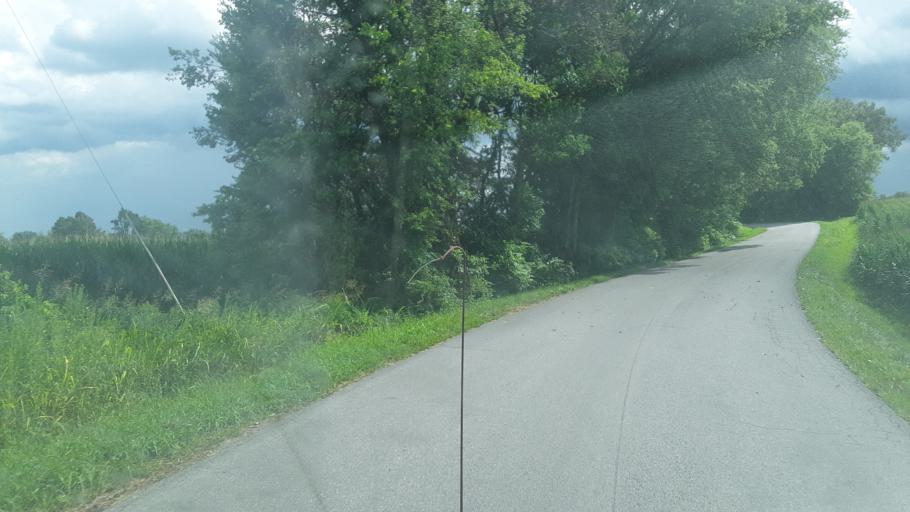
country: US
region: Kentucky
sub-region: Todd County
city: Elkton
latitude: 36.7474
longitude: -87.1693
